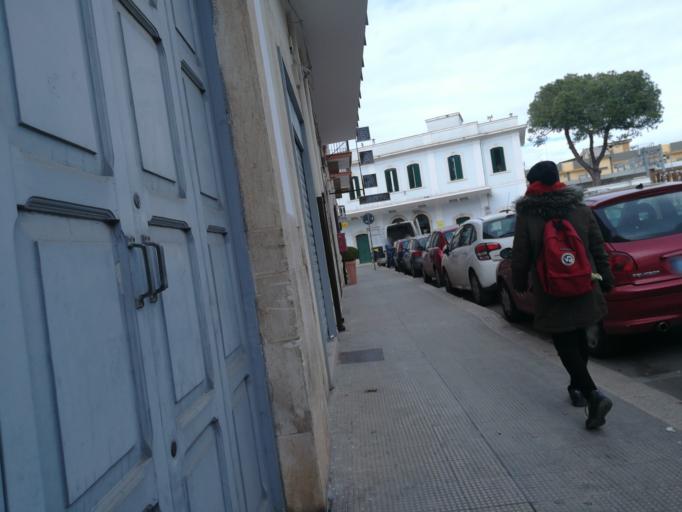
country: IT
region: Apulia
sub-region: Provincia di Bari
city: Bitonto
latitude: 41.1128
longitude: 16.6851
